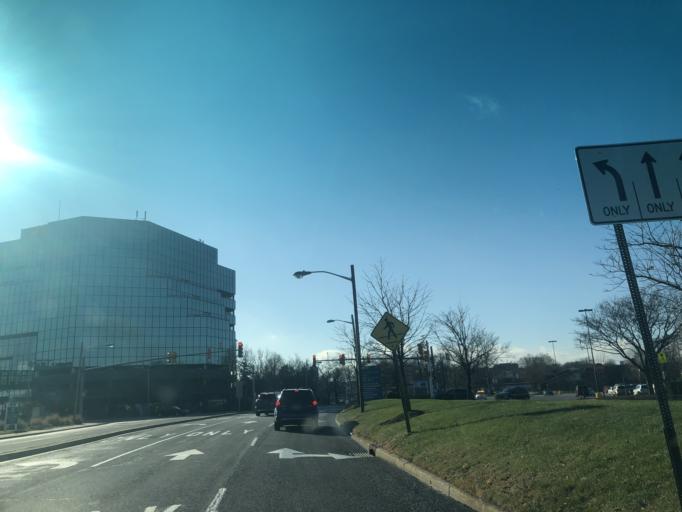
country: US
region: New Jersey
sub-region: Hudson County
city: Secaucus
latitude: 40.7920
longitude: -74.0502
